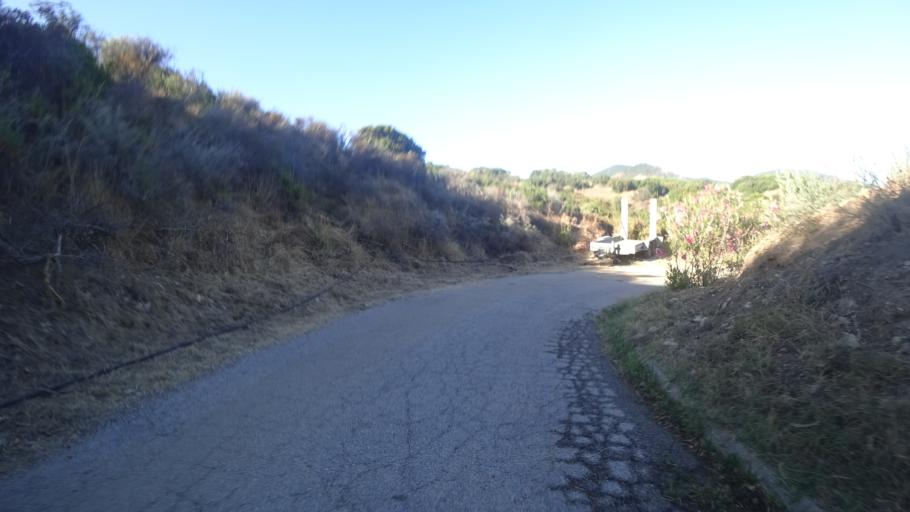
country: FR
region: Corsica
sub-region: Departement de la Corse-du-Sud
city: Alata
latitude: 41.9786
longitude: 8.6706
